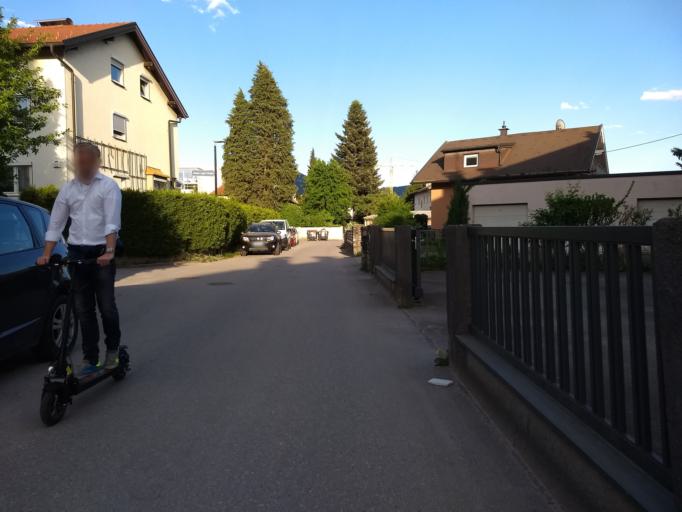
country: AT
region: Salzburg
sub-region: Politischer Bezirk Salzburg-Umgebung
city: Bergheim
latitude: 47.8103
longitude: 13.0192
